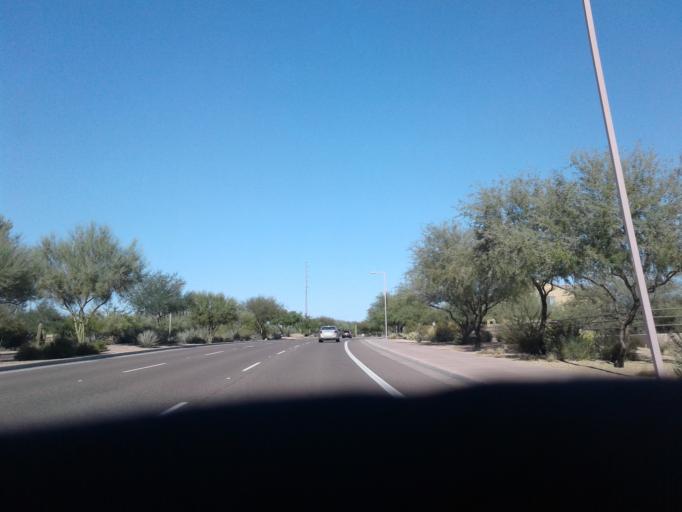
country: US
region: Arizona
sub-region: Maricopa County
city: Cave Creek
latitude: 33.6853
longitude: -111.9996
